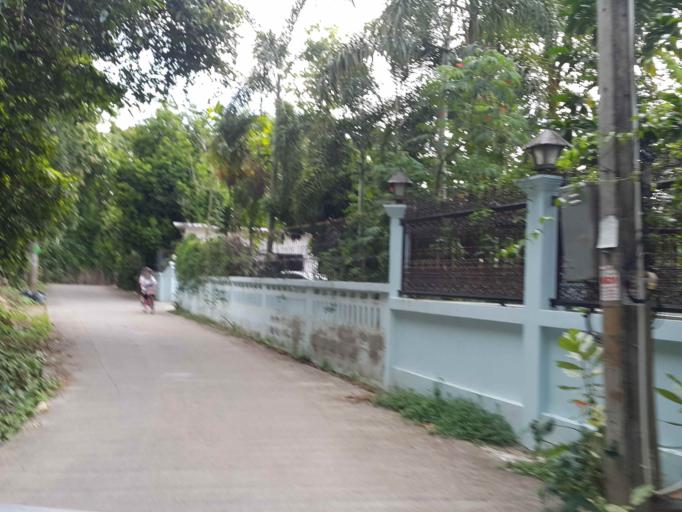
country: TH
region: Chiang Mai
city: Saraphi
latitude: 18.7107
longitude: 99.0344
